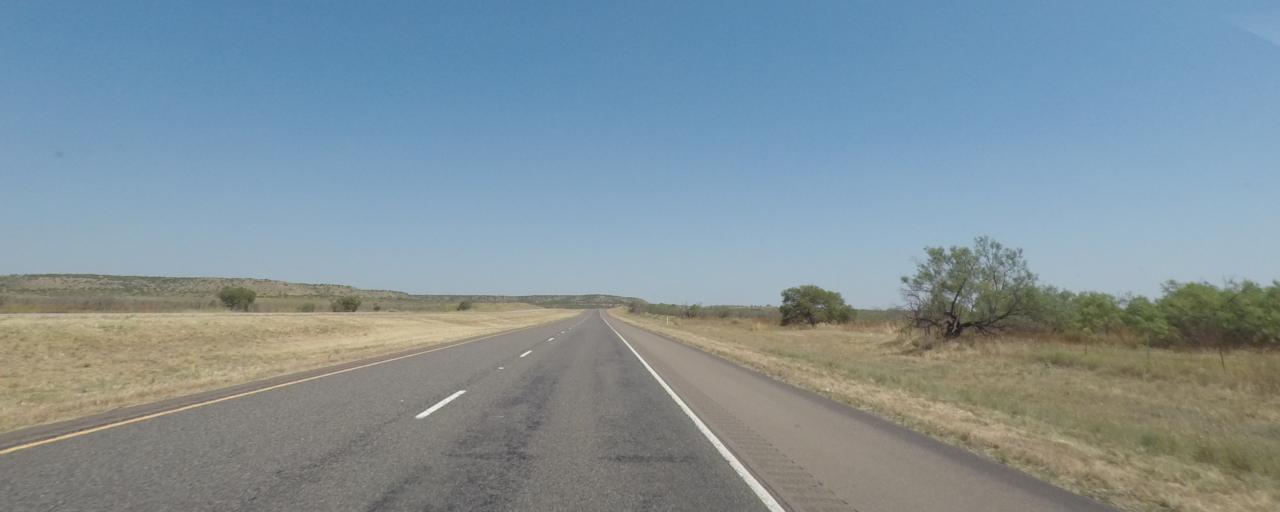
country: US
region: Texas
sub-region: Dickens County
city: Dickens
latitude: 33.6355
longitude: -100.8928
